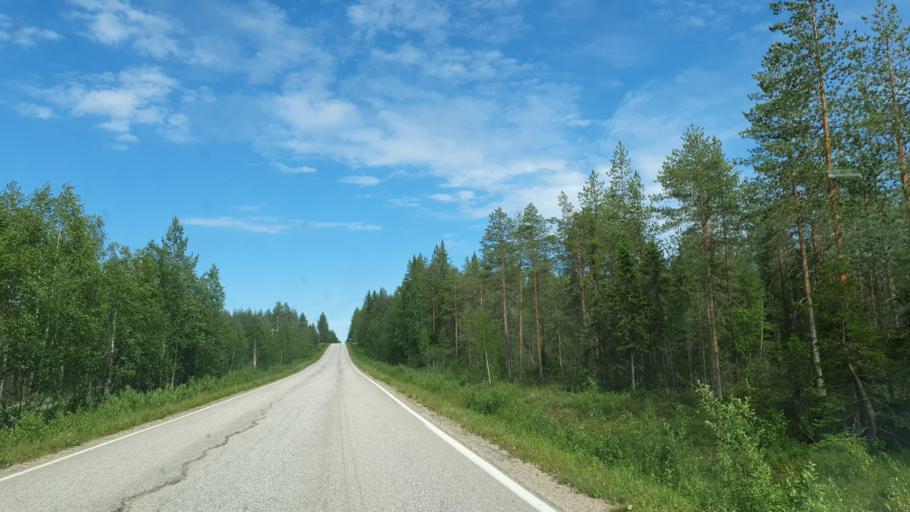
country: FI
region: Kainuu
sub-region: Kehys-Kainuu
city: Suomussalmi
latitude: 64.5833
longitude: 29.0521
